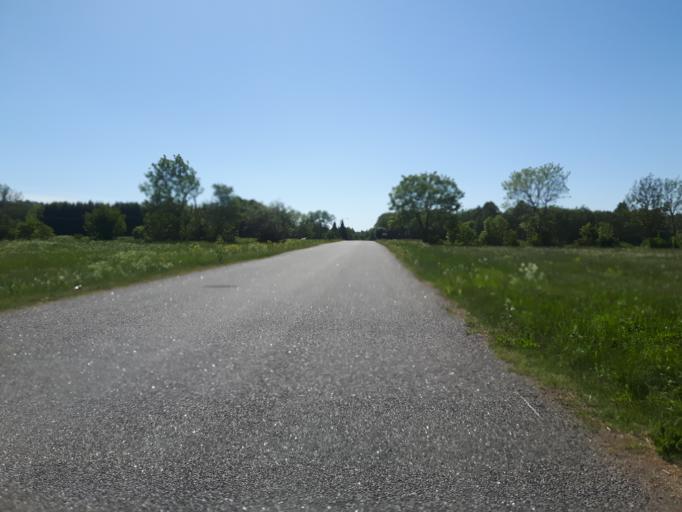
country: EE
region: Laeaene-Virumaa
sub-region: Haljala vald
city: Haljala
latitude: 59.5441
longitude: 26.1997
